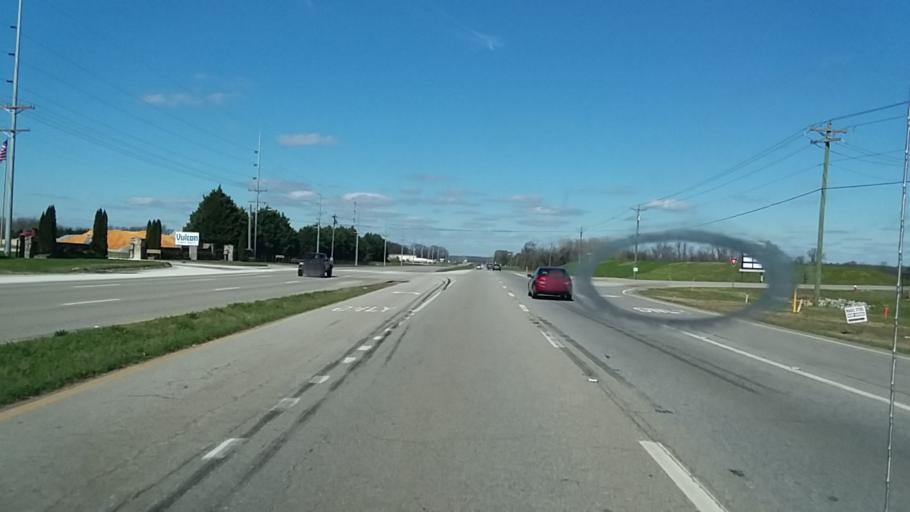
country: US
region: Alabama
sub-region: Morgan County
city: Trinity
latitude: 34.6237
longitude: -87.0823
